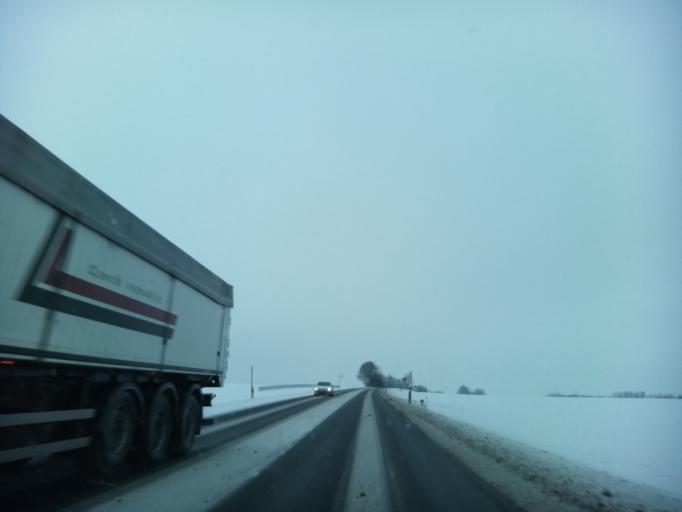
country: DE
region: Saxony
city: Grossolbersdorf
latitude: 50.7094
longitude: 13.1032
